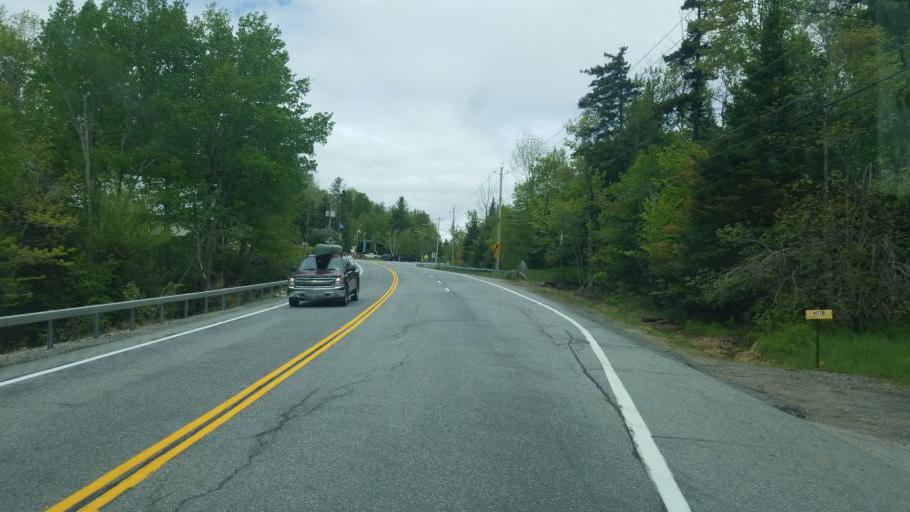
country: US
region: New York
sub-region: Franklin County
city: Tupper Lake
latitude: 43.8676
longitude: -74.4319
